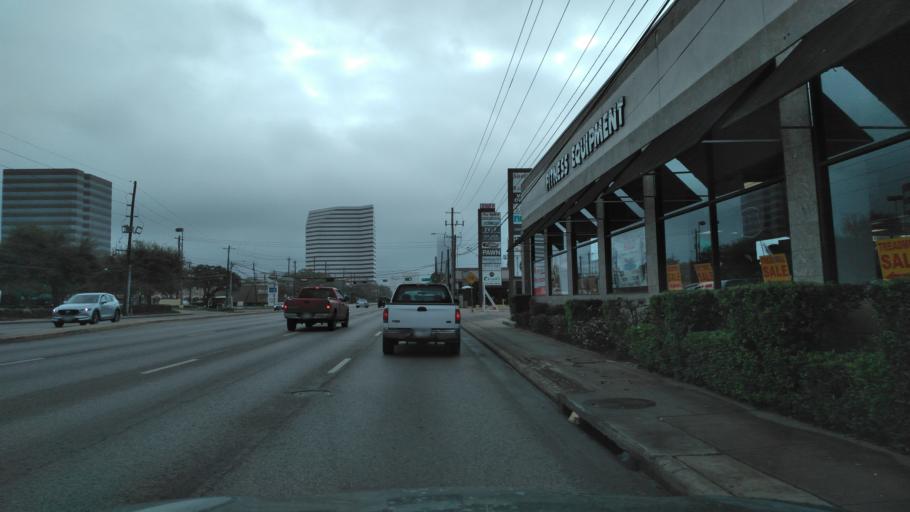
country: US
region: Texas
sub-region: Harris County
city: Hunters Creek Village
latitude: 29.7377
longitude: -95.4857
